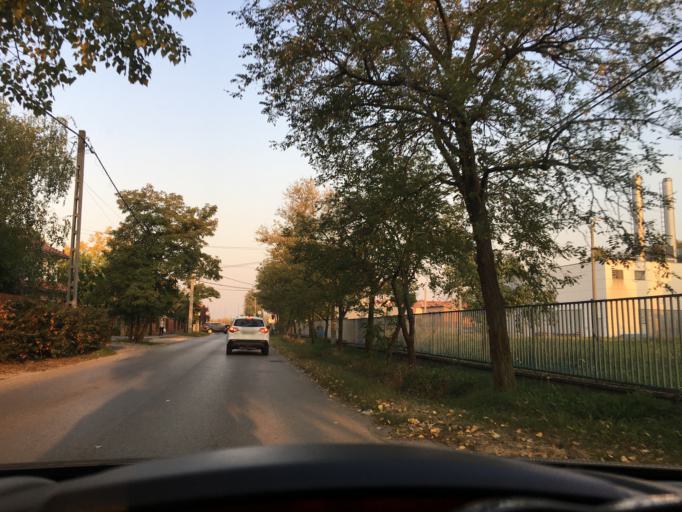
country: HU
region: Budapest
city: Budapest XVII. keruelet
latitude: 47.4768
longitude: 19.2463
